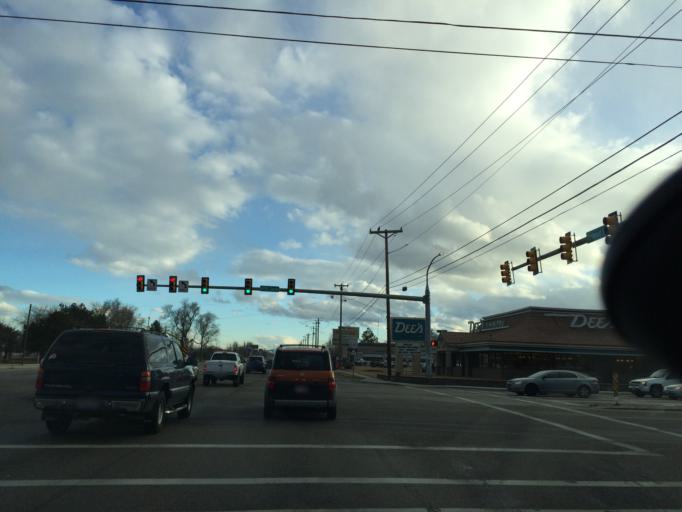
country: US
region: Utah
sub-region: Salt Lake County
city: Taylorsville
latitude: 40.6679
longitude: -111.9390
